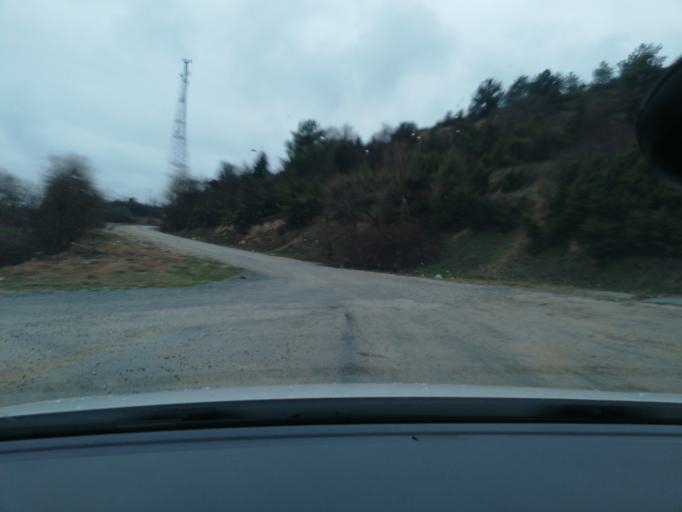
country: TR
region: Bolu
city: Bolu
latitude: 40.7645
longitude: 31.6543
